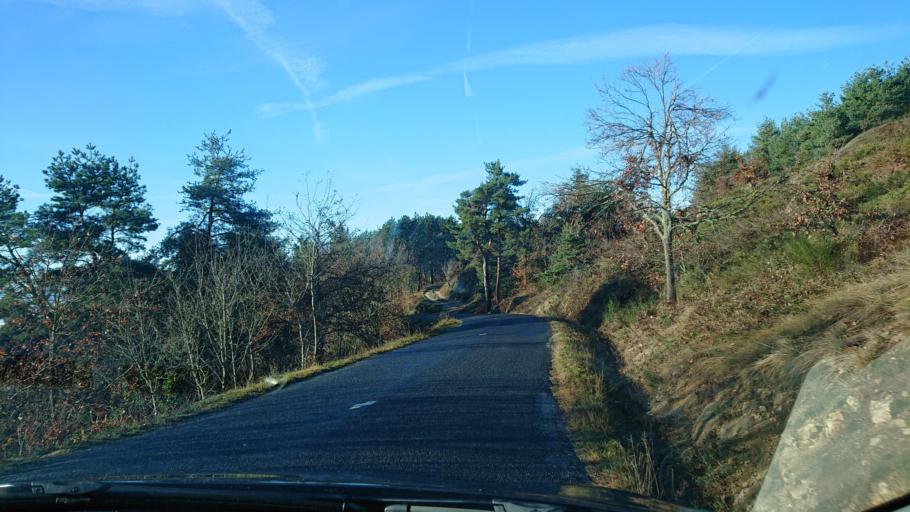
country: FR
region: Auvergne
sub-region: Departement de la Haute-Loire
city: Vorey
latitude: 45.2138
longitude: 3.9291
